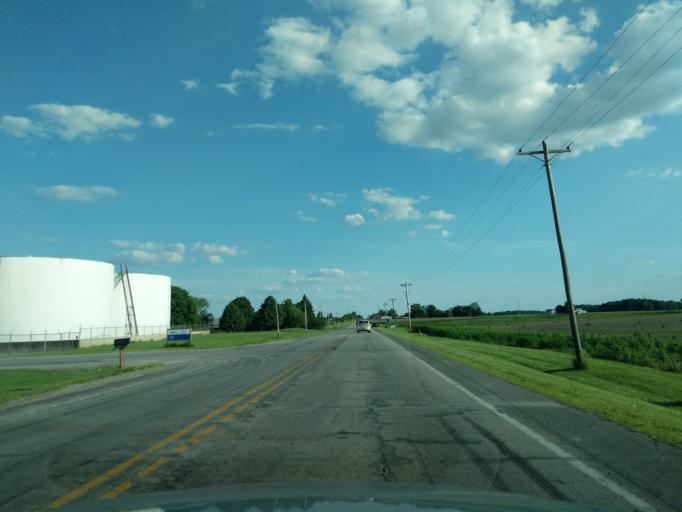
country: US
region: Indiana
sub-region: Whitley County
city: Columbia City
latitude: 41.0853
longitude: -85.4701
